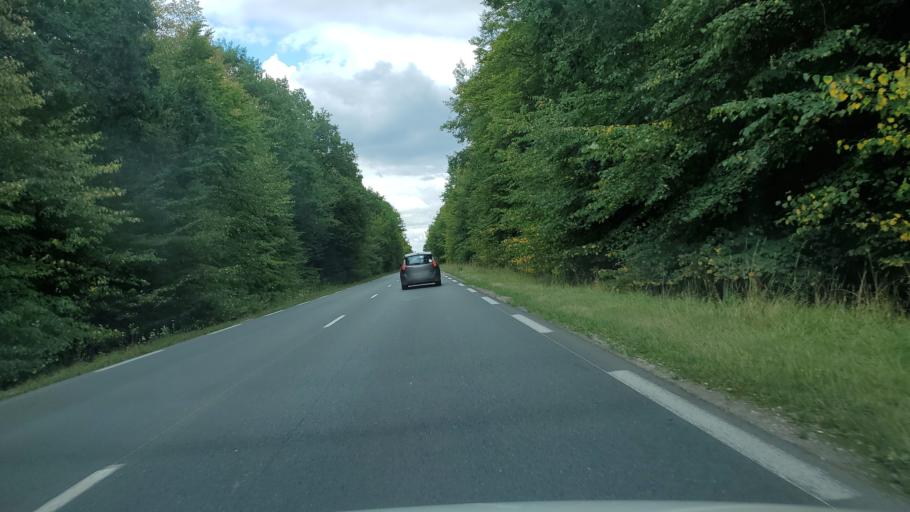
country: FR
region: Ile-de-France
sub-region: Departement de Seine-et-Marne
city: La Houssaye-en-Brie
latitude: 48.7879
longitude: 2.8764
